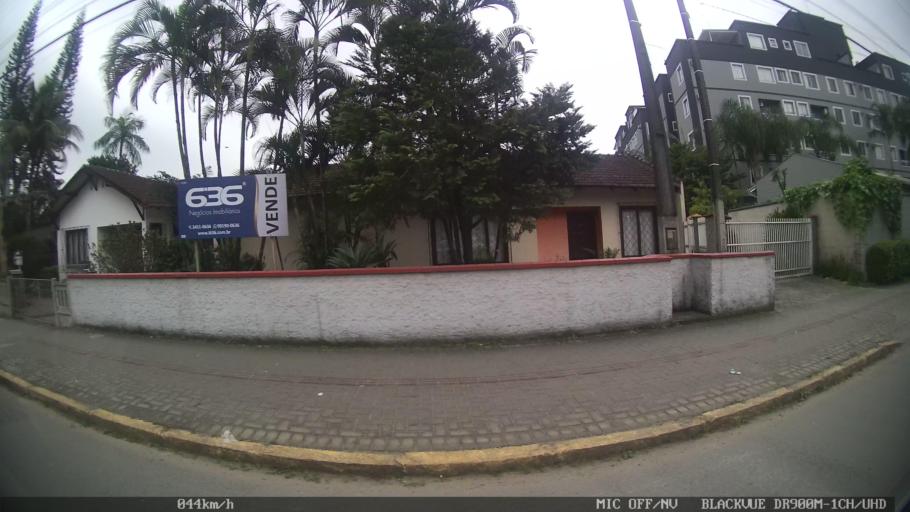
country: BR
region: Santa Catarina
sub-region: Joinville
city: Joinville
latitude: -26.2647
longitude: -48.8606
